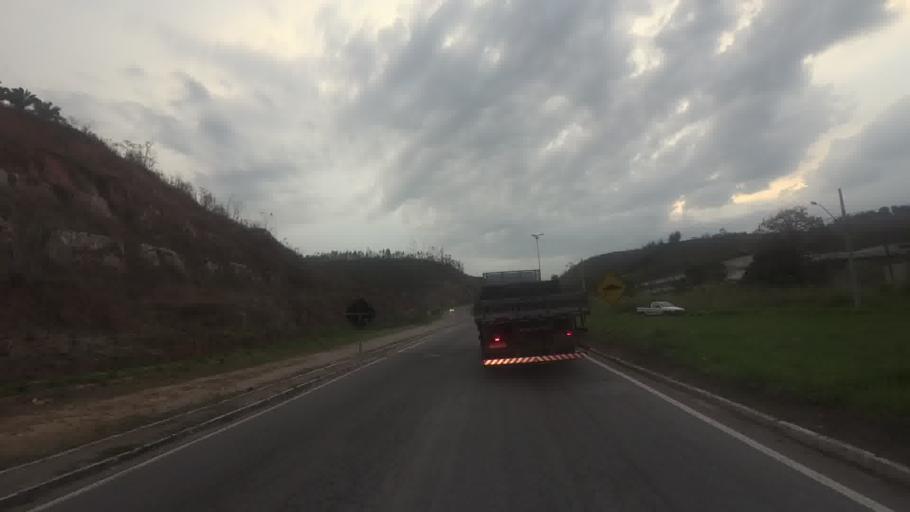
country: BR
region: Minas Gerais
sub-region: Alem Paraiba
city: Alem Paraiba
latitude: -21.8593
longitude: -42.6626
